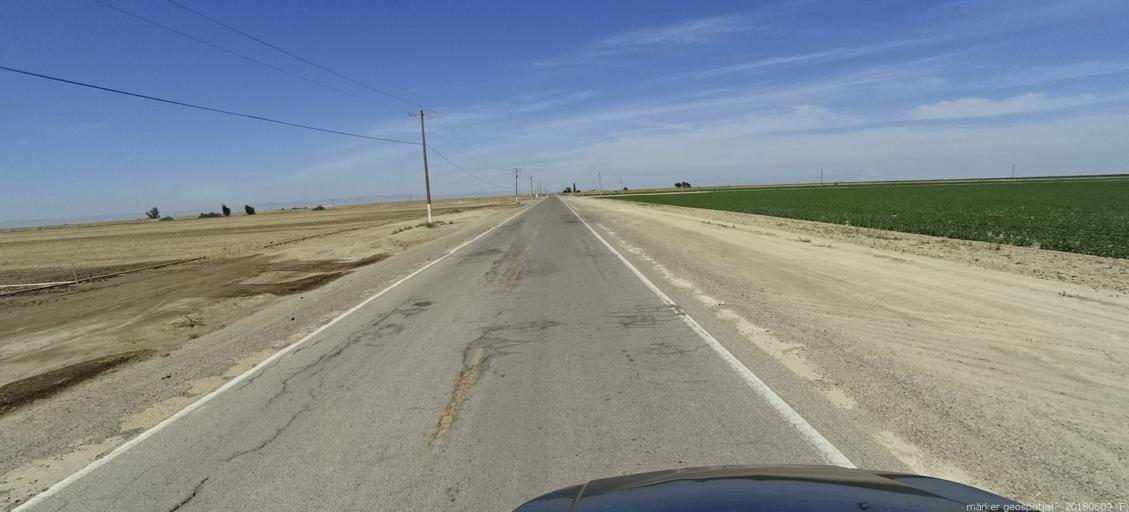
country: US
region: California
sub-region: Fresno County
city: Firebaugh
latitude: 36.9526
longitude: -120.3427
